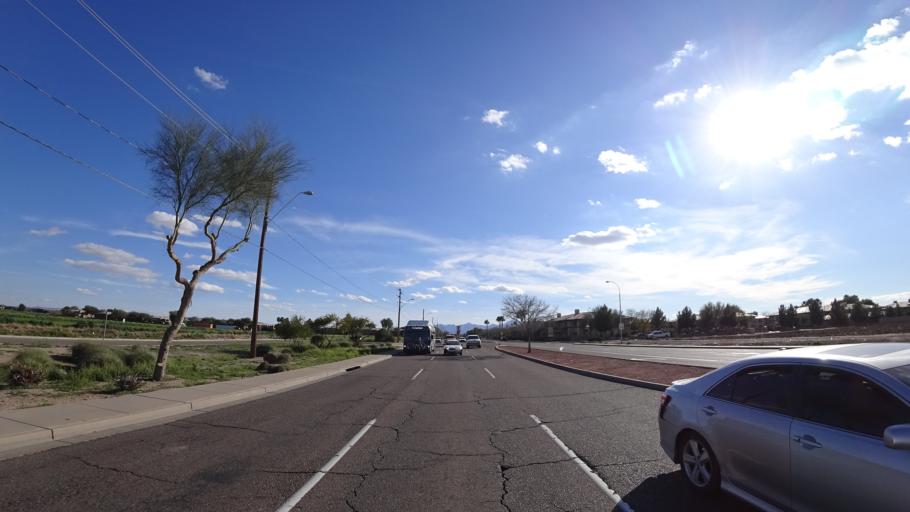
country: US
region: Arizona
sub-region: Maricopa County
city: Tolleson
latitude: 33.4786
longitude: -112.2377
